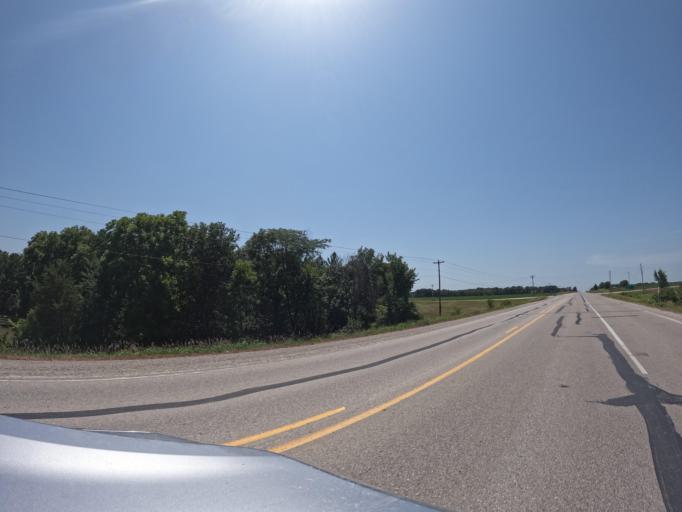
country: US
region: Iowa
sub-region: Henry County
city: Mount Pleasant
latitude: 40.9671
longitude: -91.6106
